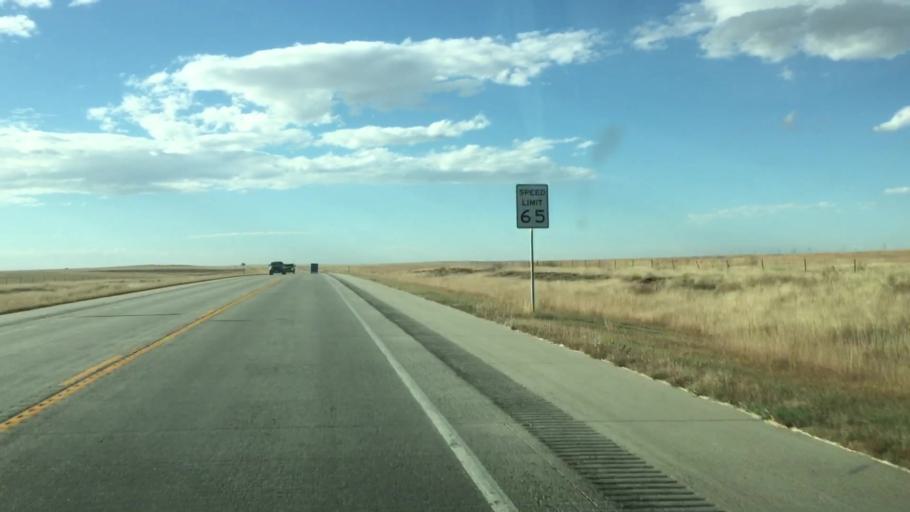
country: US
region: Colorado
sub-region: Lincoln County
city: Hugo
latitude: 39.1870
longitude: -103.5558
